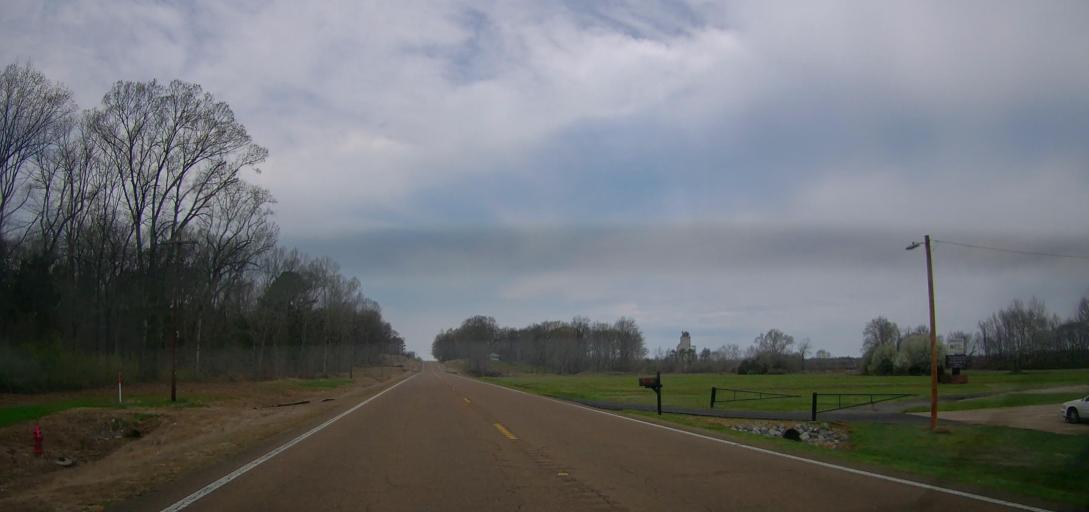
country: US
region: Mississippi
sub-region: Marshall County
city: Byhalia
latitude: 34.8573
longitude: -89.6468
